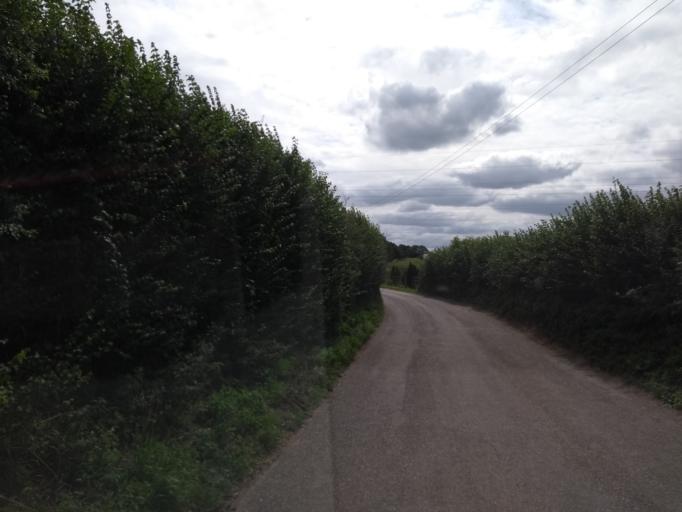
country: GB
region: England
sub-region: Somerset
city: North Petherton
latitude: 51.0854
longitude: -3.0108
